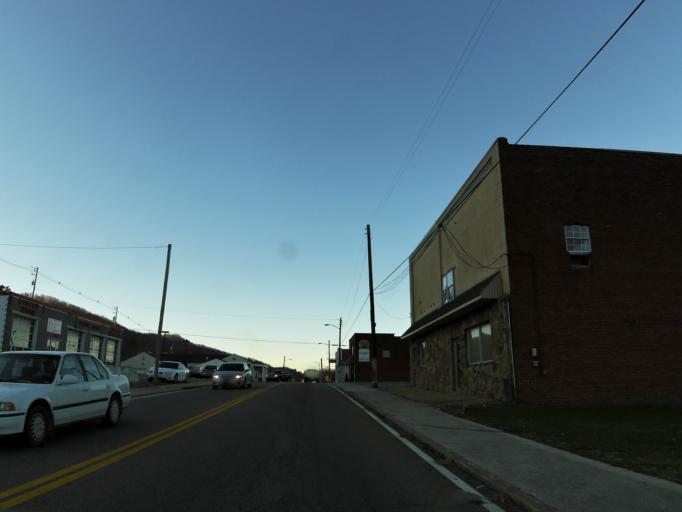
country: US
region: Tennessee
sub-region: Anderson County
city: Rocky Top
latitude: 36.2166
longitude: -84.1536
